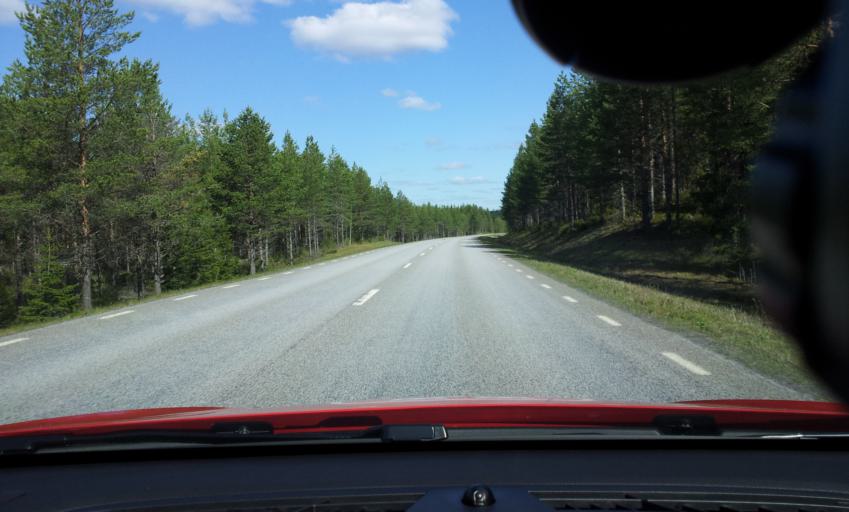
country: SE
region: Jaemtland
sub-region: Krokoms Kommun
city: Valla
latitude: 63.2809
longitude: 13.9334
